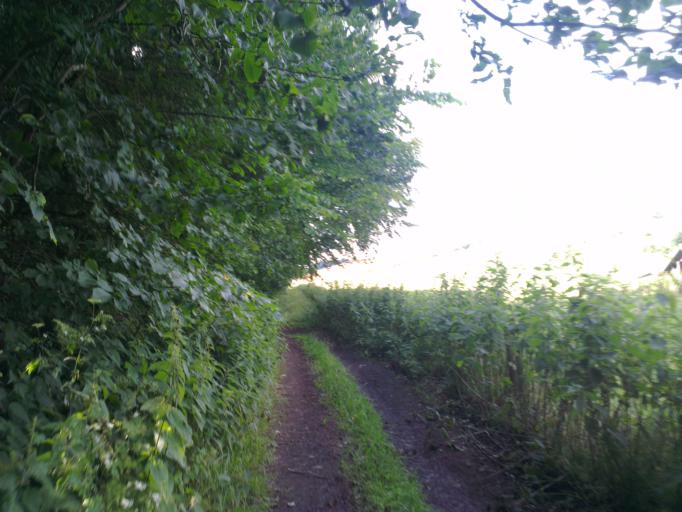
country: DK
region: Zealand
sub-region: Lejre Kommune
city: Ejby
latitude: 55.7365
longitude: 11.8793
